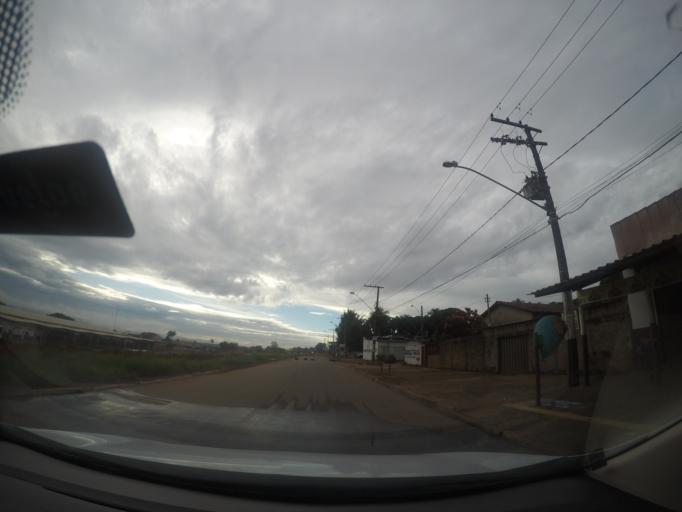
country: BR
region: Goias
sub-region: Goiania
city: Goiania
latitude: -16.6068
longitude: -49.3185
